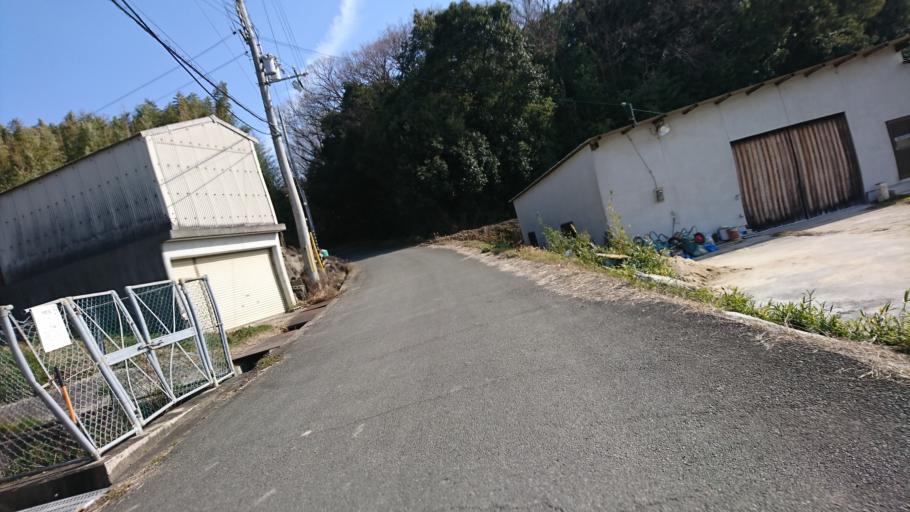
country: JP
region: Hyogo
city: Kakogawacho-honmachi
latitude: 34.8213
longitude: 134.8541
